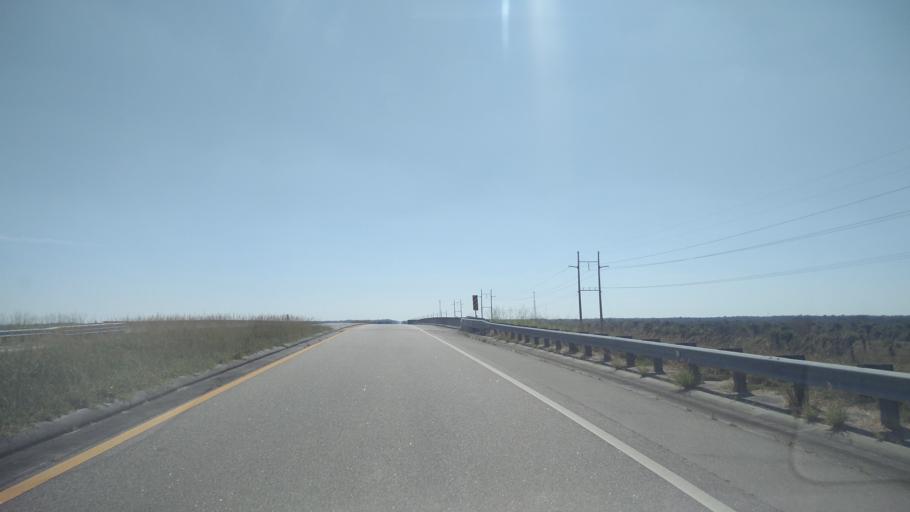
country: US
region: Florida
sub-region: Collier County
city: Immokalee
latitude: 26.1555
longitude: -81.3452
